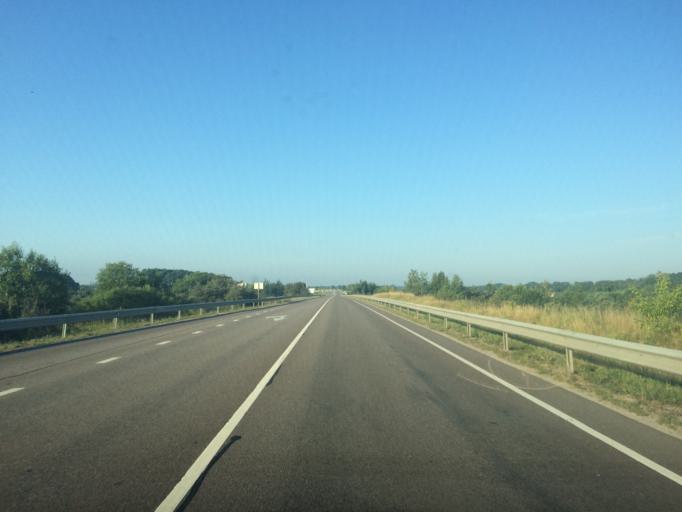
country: LT
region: Vilnius County
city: Ukmerge
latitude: 55.3292
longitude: 24.8839
